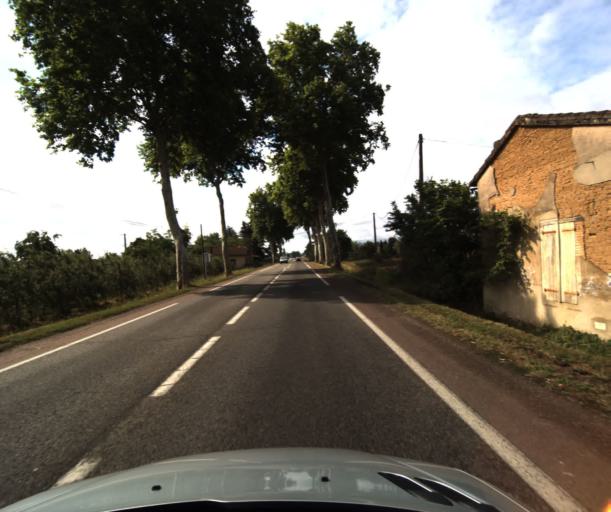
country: FR
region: Midi-Pyrenees
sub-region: Departement du Tarn-et-Garonne
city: Castelsarrasin
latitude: 44.0677
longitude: 1.0957
